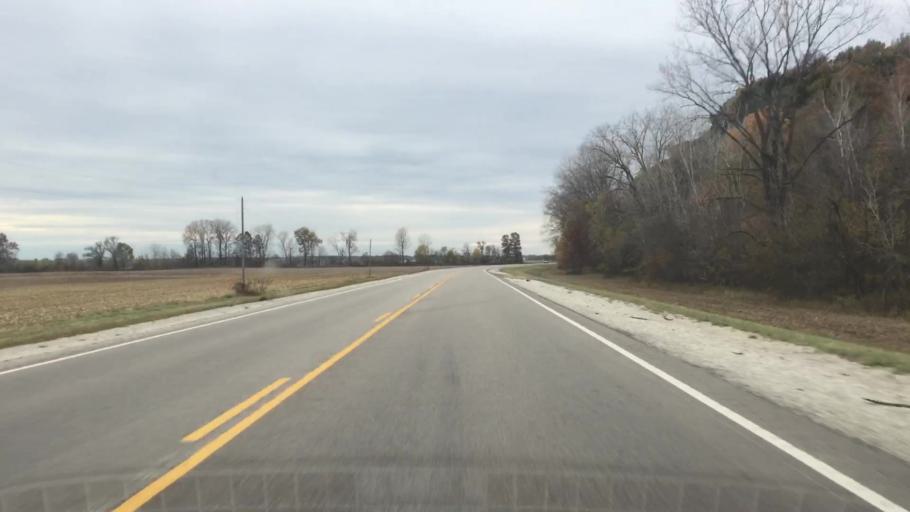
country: US
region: Missouri
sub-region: Callaway County
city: Holts Summit
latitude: 38.5836
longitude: -92.1129
